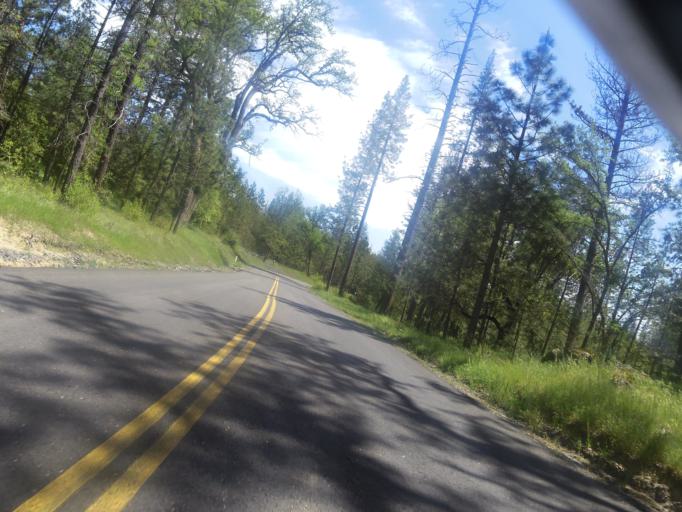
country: US
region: California
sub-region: Madera County
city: Ahwahnee
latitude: 37.4693
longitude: -119.7983
